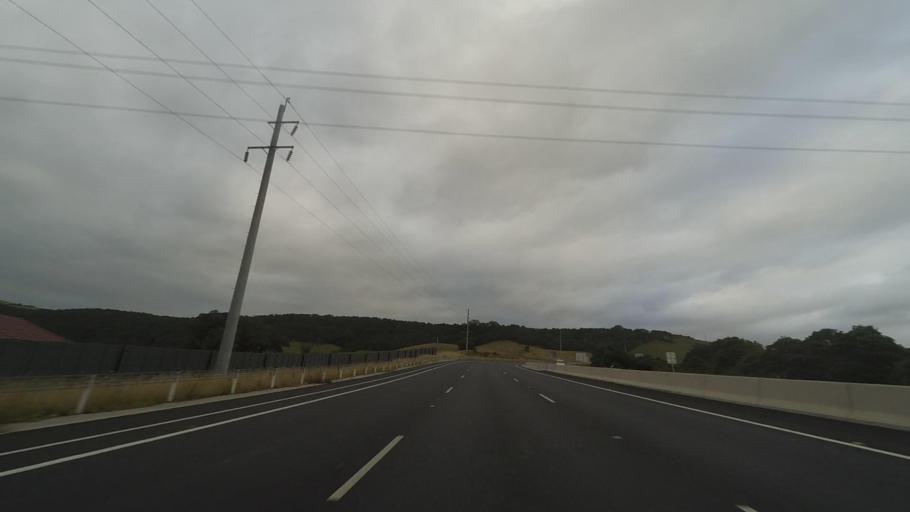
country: AU
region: New South Wales
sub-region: Kiama
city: Gerringong
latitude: -34.7136
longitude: 150.8355
